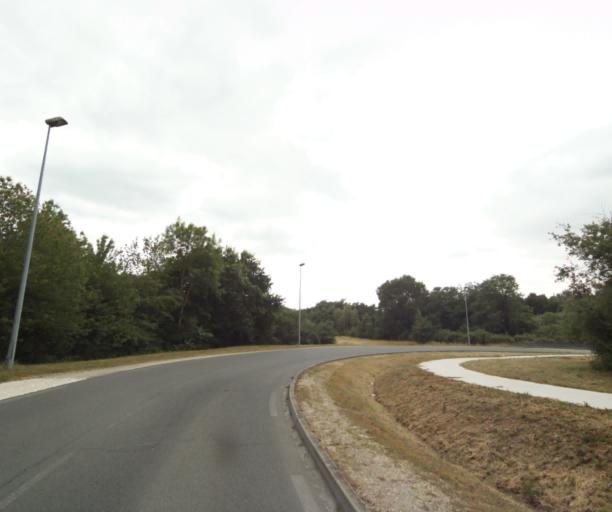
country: FR
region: Centre
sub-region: Departement du Loiret
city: Saint-Jean-de-la-Ruelle
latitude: 47.9278
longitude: 1.8505
